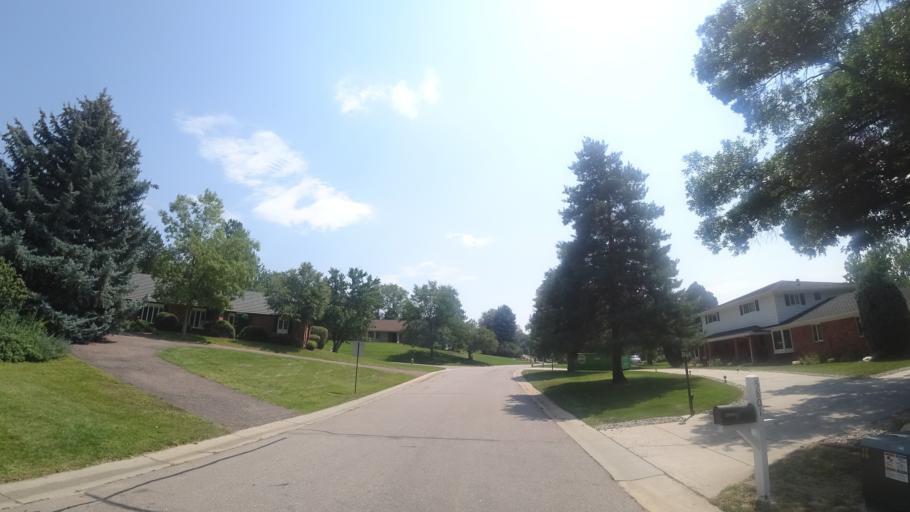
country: US
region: Colorado
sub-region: Arapahoe County
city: Greenwood Village
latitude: 39.6118
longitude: -104.9735
